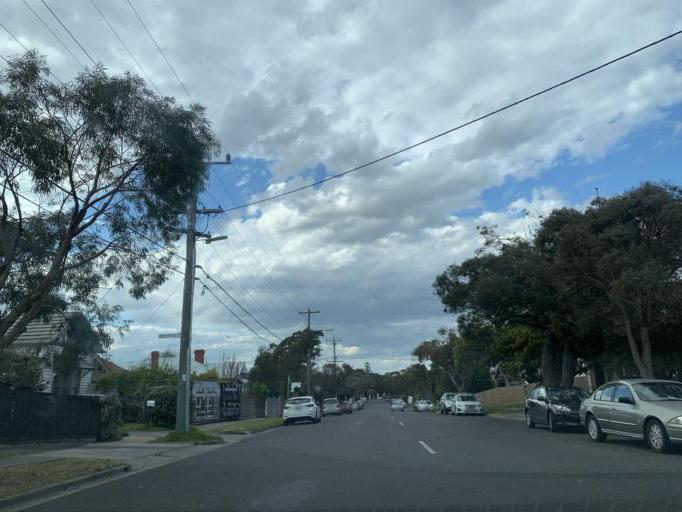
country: AU
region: Victoria
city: Hampton
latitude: -37.9514
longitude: 145.0059
